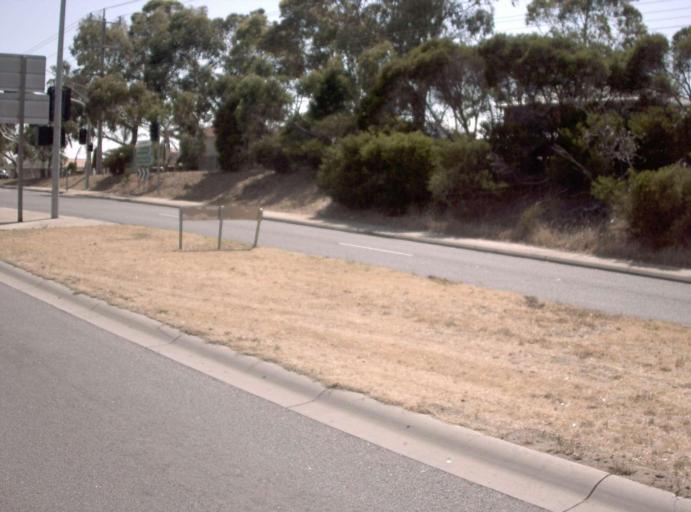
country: AU
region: Victoria
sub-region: Greater Dandenong
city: Noble Park North
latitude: -37.9344
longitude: 145.1930
